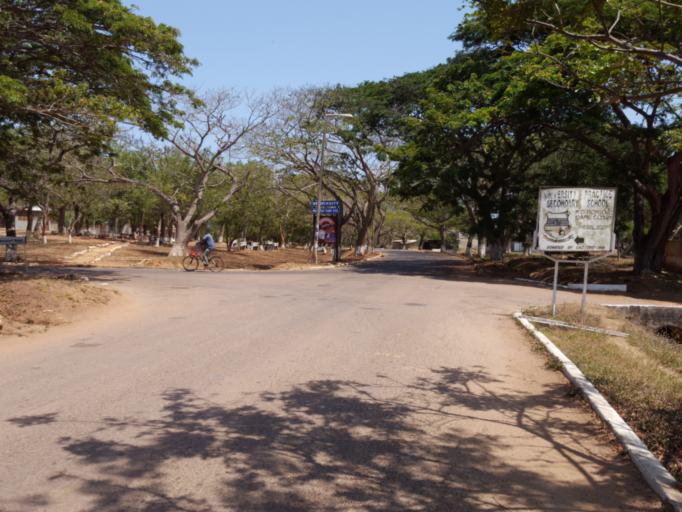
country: GH
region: Central
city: Cape Coast
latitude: 5.1247
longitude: -1.2874
